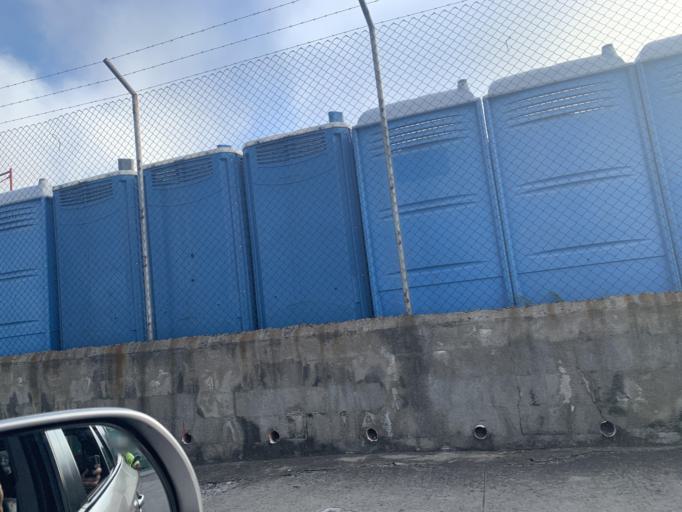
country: GT
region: Guatemala
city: Guatemala City
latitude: 14.5933
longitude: -90.5504
